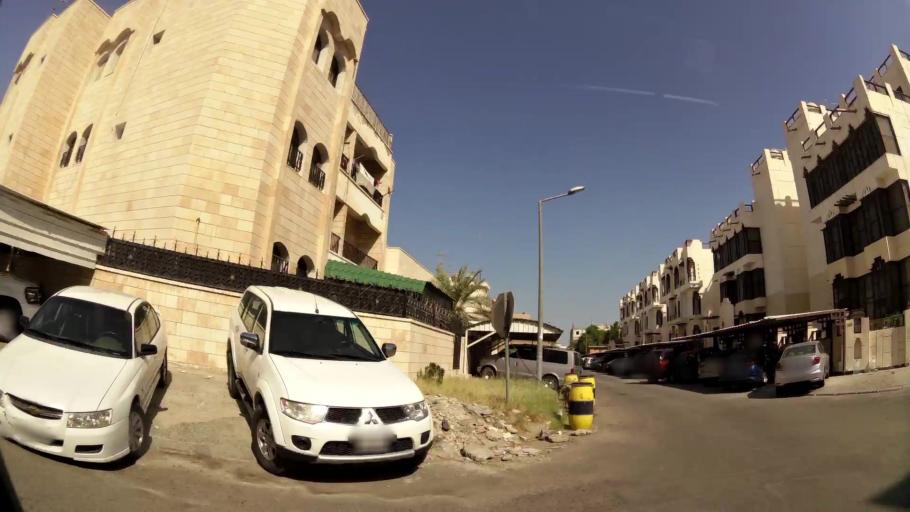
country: KW
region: Muhafazat Hawalli
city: Salwa
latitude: 29.2814
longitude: 48.0799
